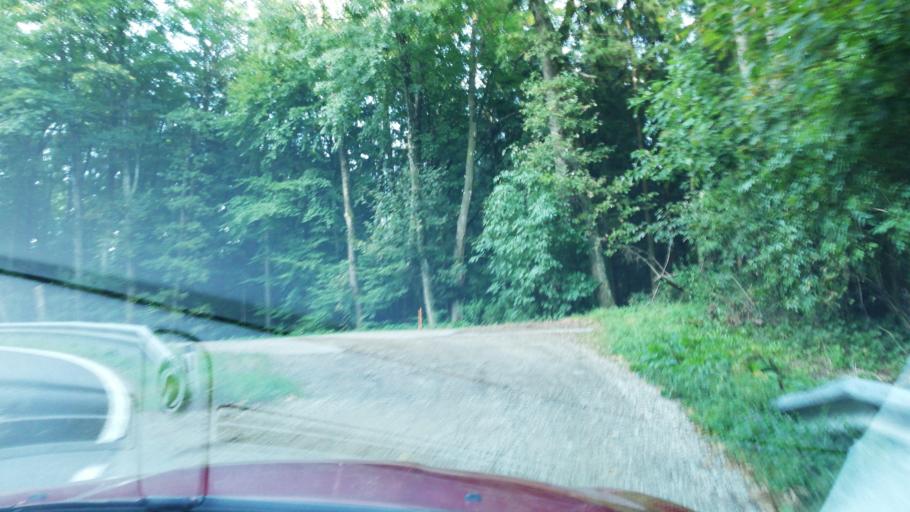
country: AT
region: Upper Austria
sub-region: Politischer Bezirk Vocklabruck
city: Redleiten
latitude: 48.1195
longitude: 13.5660
